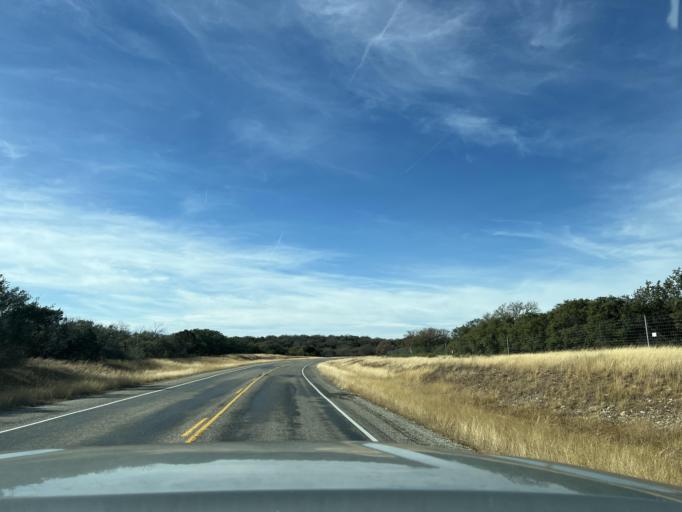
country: US
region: Texas
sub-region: Eastland County
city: Cisco
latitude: 32.4608
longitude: -99.0097
